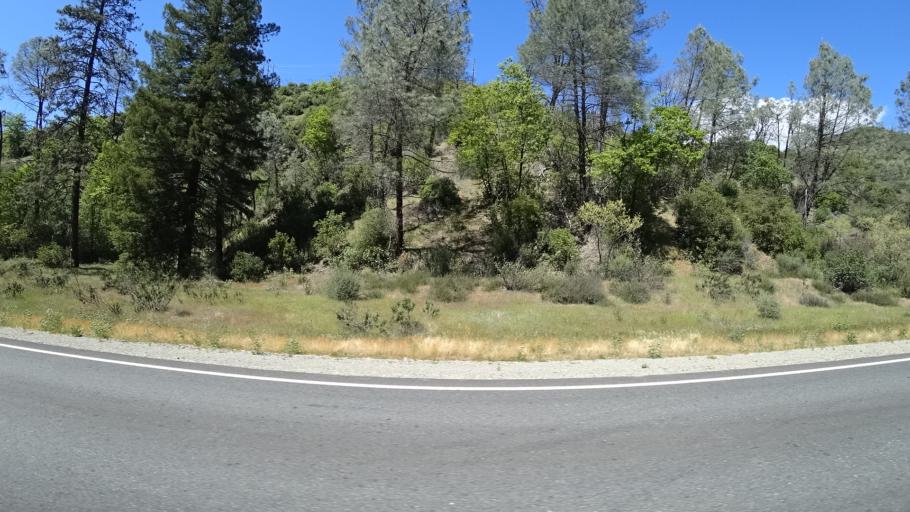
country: US
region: California
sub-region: Trinity County
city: Weaverville
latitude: 40.7306
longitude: -123.0316
